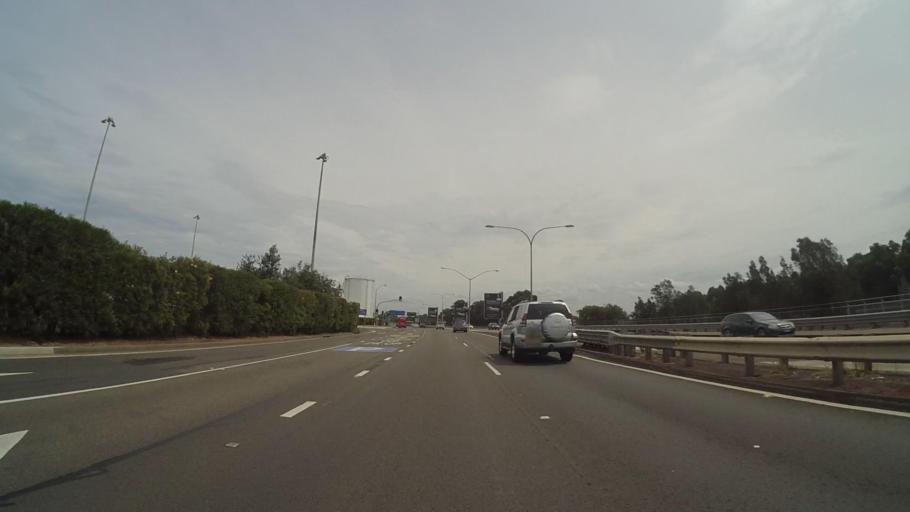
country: AU
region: New South Wales
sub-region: Rockdale
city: Arncliffe
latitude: -33.9293
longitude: 151.1659
